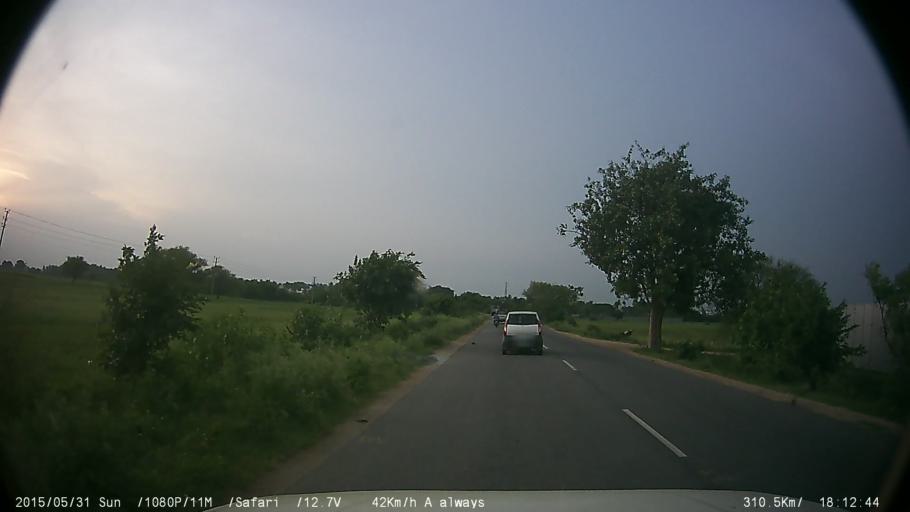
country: IN
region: Karnataka
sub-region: Mysore
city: Nanjangud
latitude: 12.0978
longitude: 76.6720
